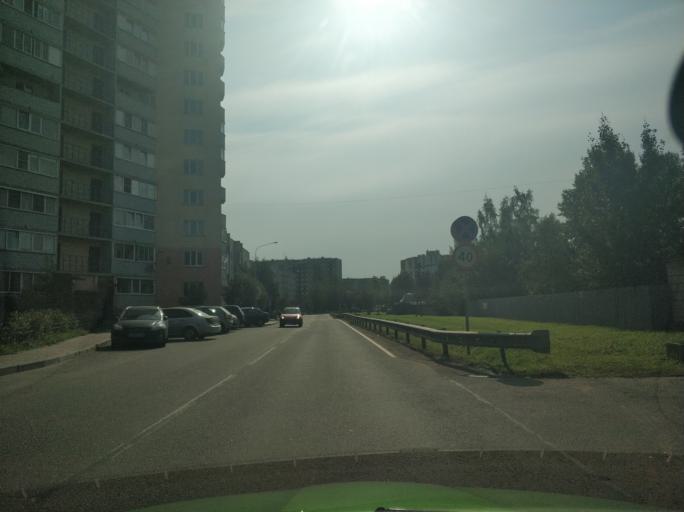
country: RU
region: Leningrad
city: Murino
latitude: 60.0467
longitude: 30.4612
